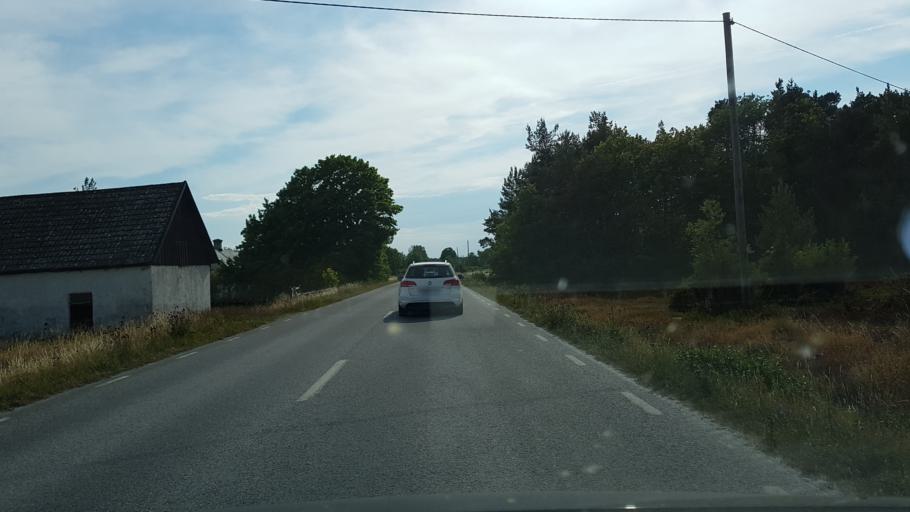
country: SE
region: Gotland
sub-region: Gotland
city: Visby
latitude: 57.6348
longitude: 18.4518
